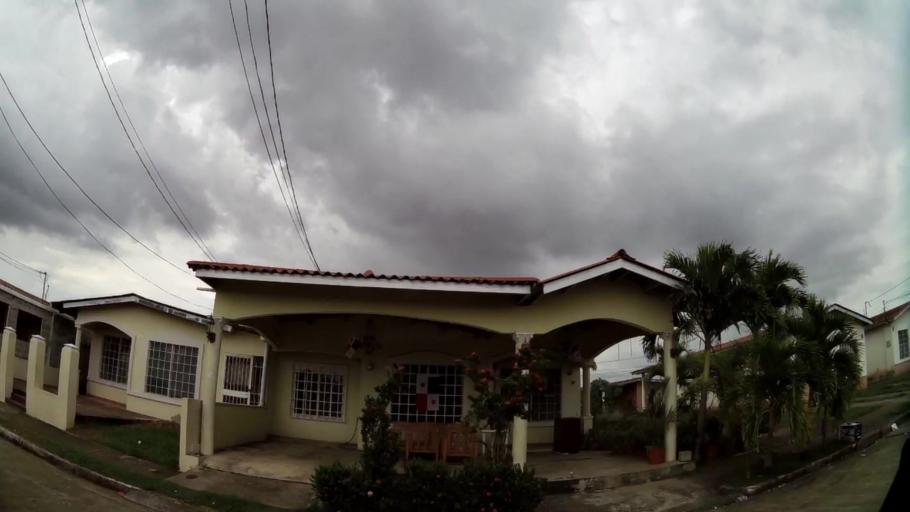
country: PA
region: Panama
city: Tocumen
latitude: 9.0453
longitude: -79.4063
